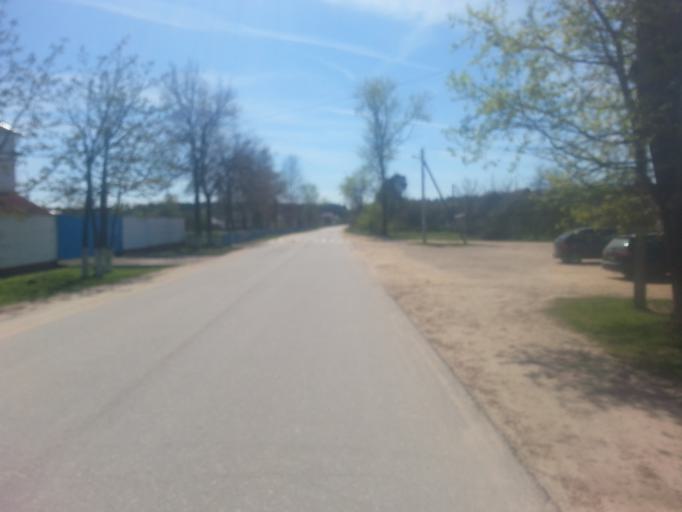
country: BY
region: Minsk
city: Narach
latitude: 54.9309
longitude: 26.6850
